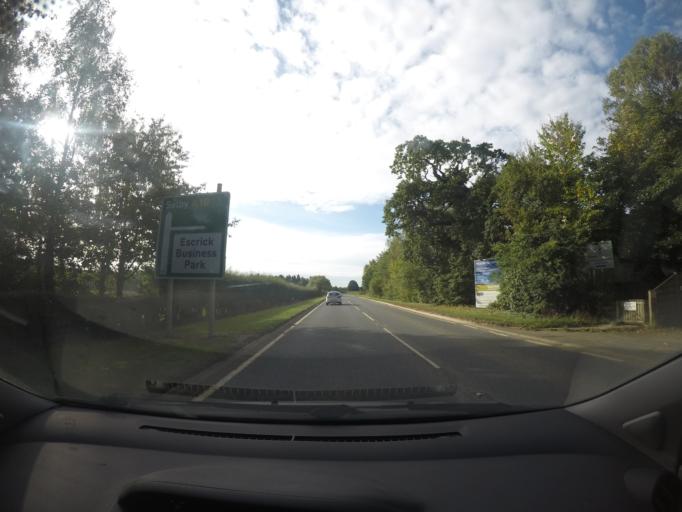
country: GB
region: England
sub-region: North Yorkshire
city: Riccall
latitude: 53.8553
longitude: -1.0495
